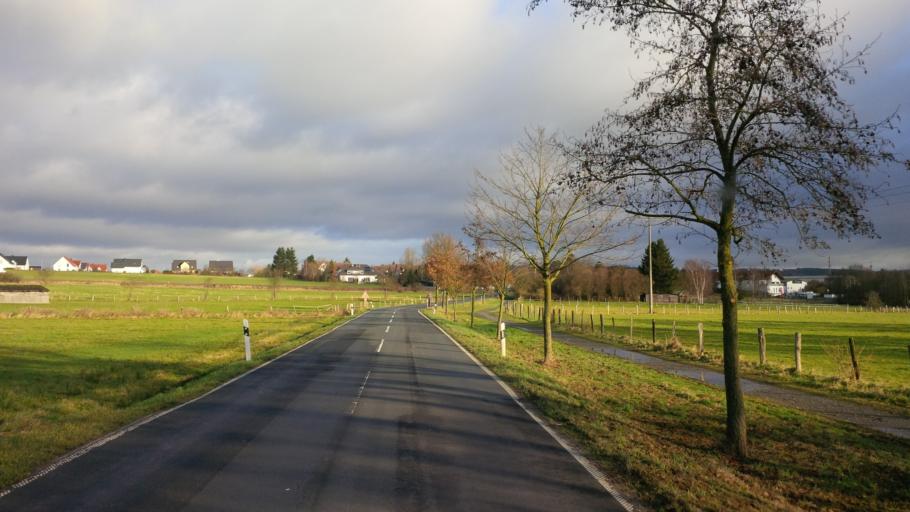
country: DE
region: Hesse
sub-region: Regierungsbezirk Darmstadt
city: Wehrheim
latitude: 50.2937
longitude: 8.5606
